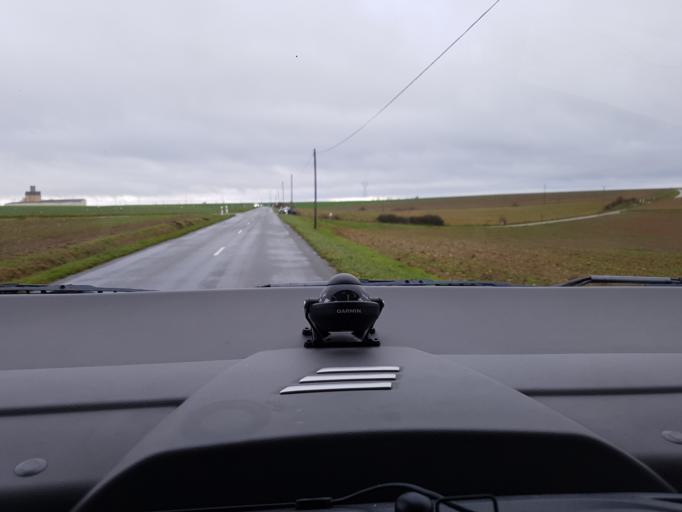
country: FR
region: Haute-Normandie
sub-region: Departement de l'Eure
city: Pont-Saint-Pierre
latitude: 49.3068
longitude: 1.3166
